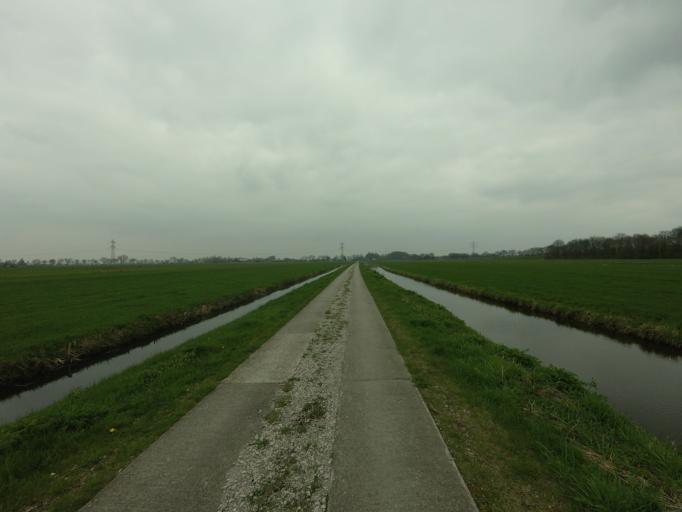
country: NL
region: Utrecht
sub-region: Gemeente De Bilt
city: De Bilt
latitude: 52.1421
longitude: 5.1525
